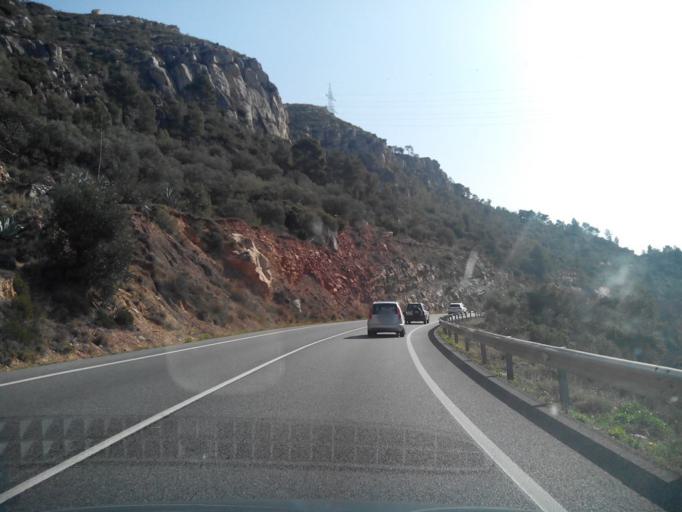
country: ES
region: Catalonia
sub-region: Provincia de Tarragona
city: Alcover
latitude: 41.3129
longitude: 1.1879
